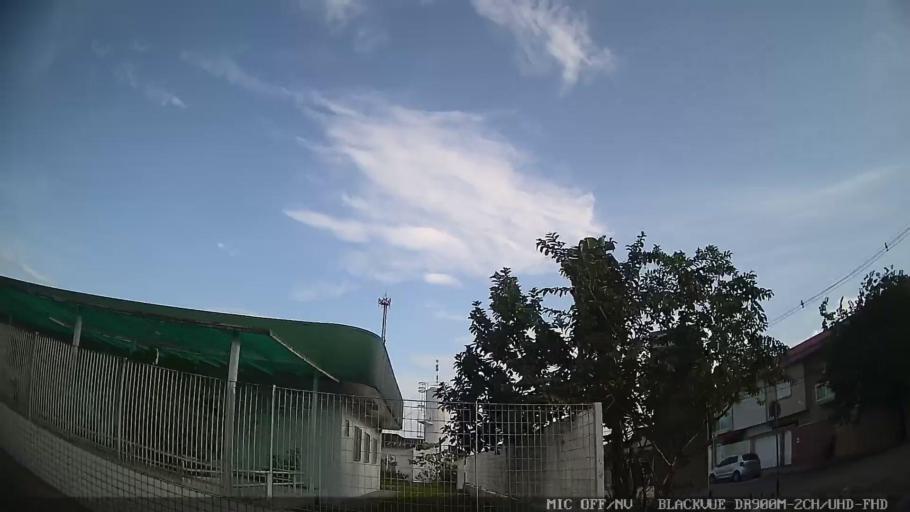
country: BR
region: Sao Paulo
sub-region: Cubatao
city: Cubatao
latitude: -23.8995
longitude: -46.4242
